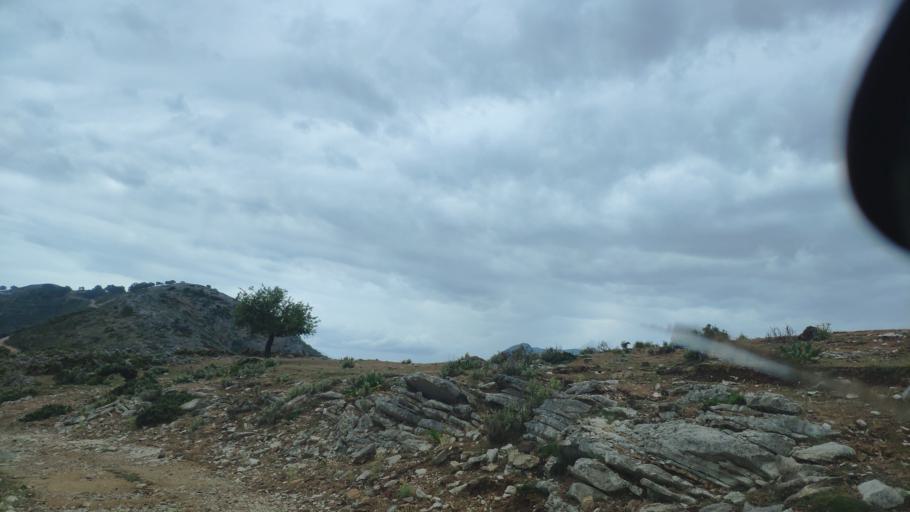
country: GR
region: West Greece
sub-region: Nomos Aitolias kai Akarnanias
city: Archontochorion
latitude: 38.6788
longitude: 21.0169
